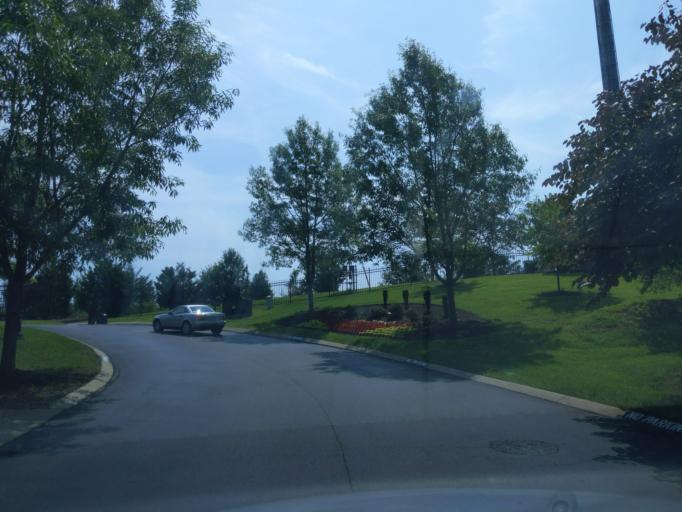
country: US
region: Tennessee
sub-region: Williamson County
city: Brentwood Estates
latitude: 36.0393
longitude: -86.7467
